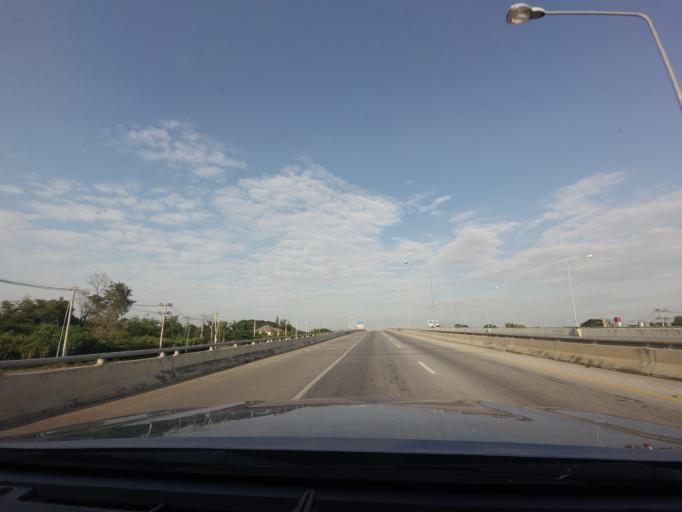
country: TH
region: Nakhon Sawan
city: Nakhon Sawan
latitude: 15.7512
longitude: 100.0835
